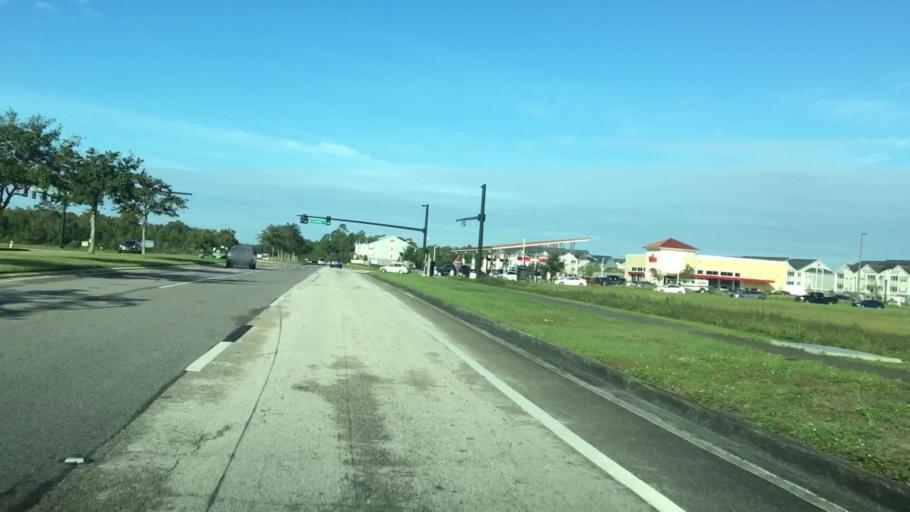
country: US
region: Florida
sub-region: Orange County
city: Azalea Park
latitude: 28.4784
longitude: -81.2460
